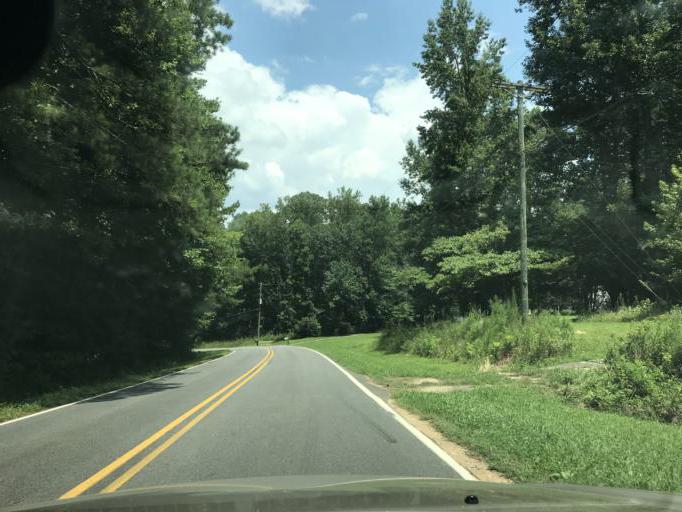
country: US
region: Georgia
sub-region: Dawson County
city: Dawsonville
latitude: 34.3252
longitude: -84.1714
